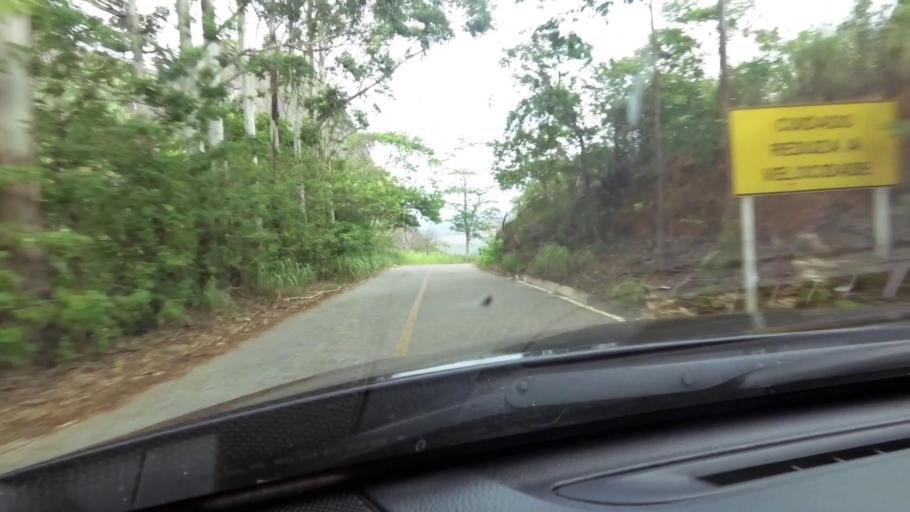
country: BR
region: Espirito Santo
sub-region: Guarapari
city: Guarapari
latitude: -20.6025
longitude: -40.5365
